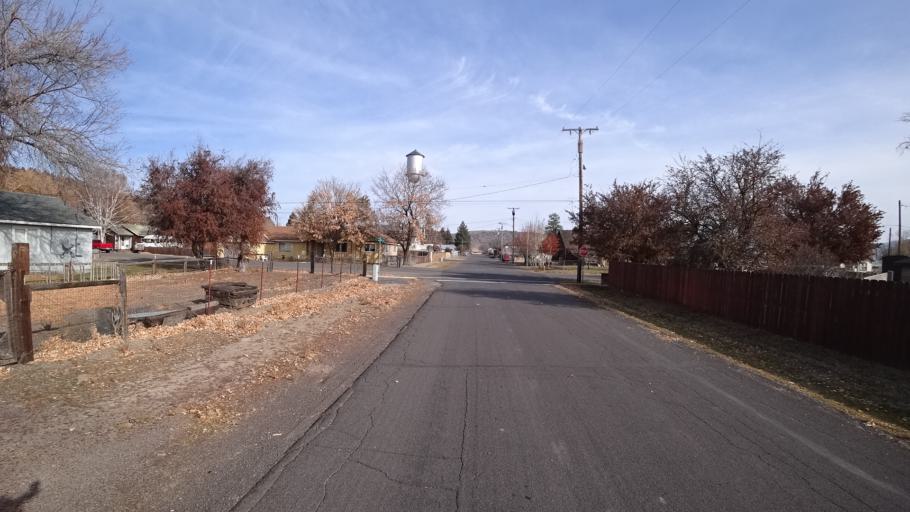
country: US
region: Oregon
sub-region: Klamath County
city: Klamath Falls
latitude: 41.9657
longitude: -121.9217
